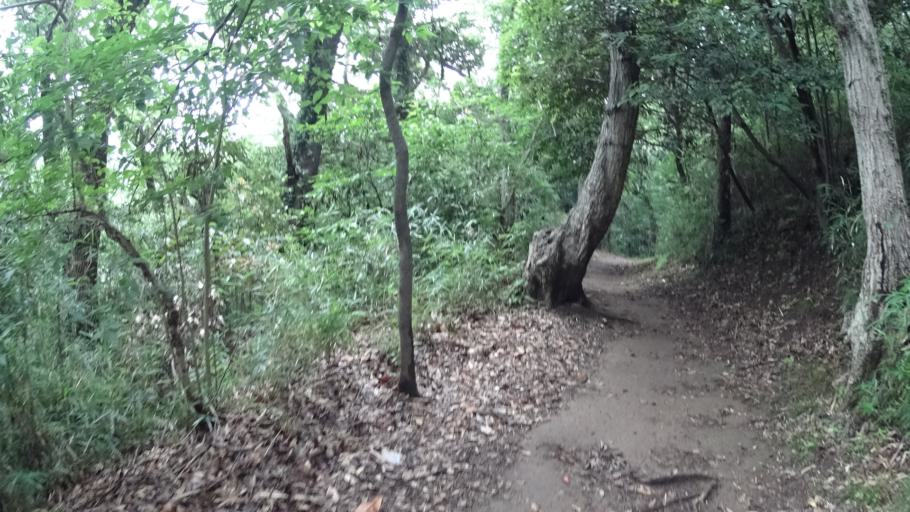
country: JP
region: Kanagawa
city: Zushi
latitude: 35.3575
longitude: 139.6076
